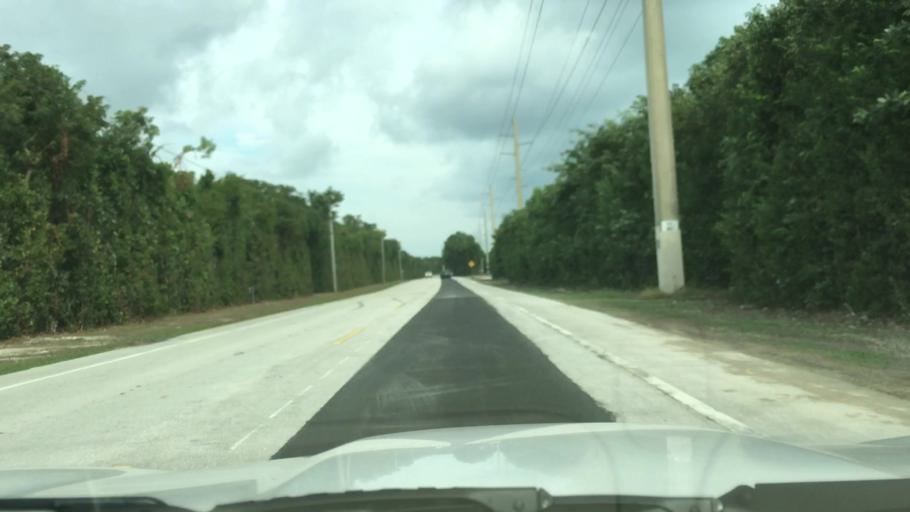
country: US
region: Florida
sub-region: Monroe County
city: North Key Largo
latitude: 25.2181
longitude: -80.3364
